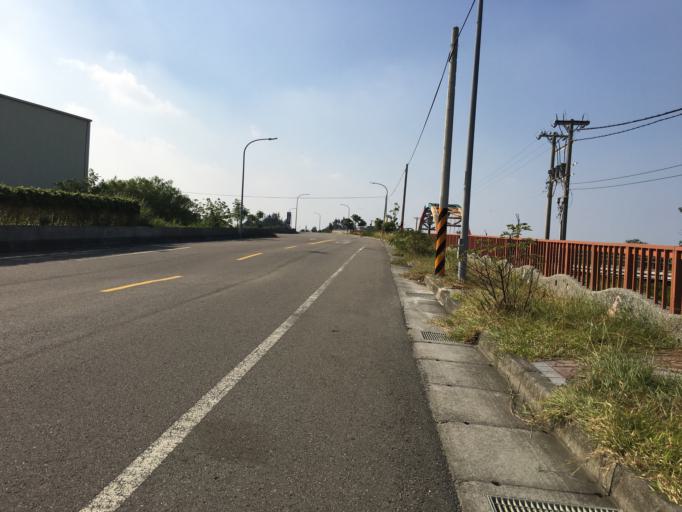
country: TW
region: Taiwan
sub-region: Hsinchu
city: Hsinchu
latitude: 24.8028
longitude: 120.9175
